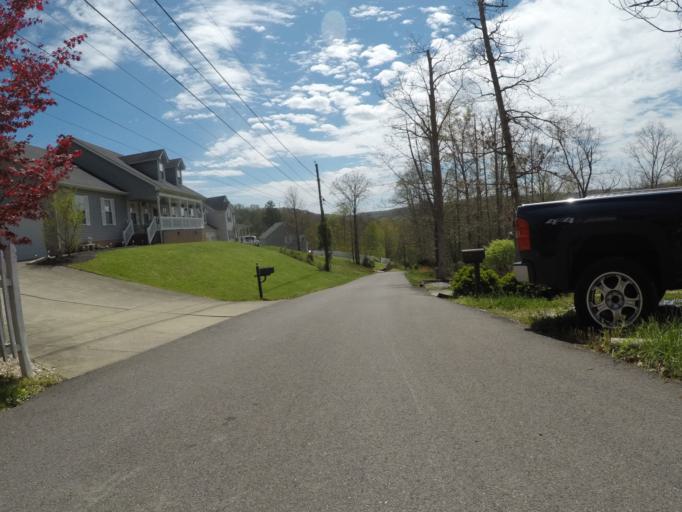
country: US
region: Ohio
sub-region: Lawrence County
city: Burlington
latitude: 38.3737
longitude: -82.5128
